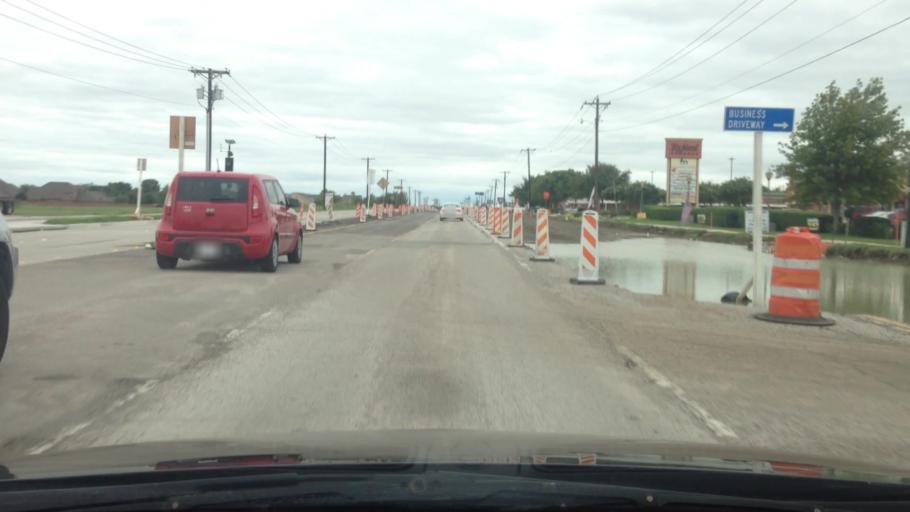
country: US
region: Texas
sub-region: Tarrant County
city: Watauga
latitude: 32.8744
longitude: -97.2379
